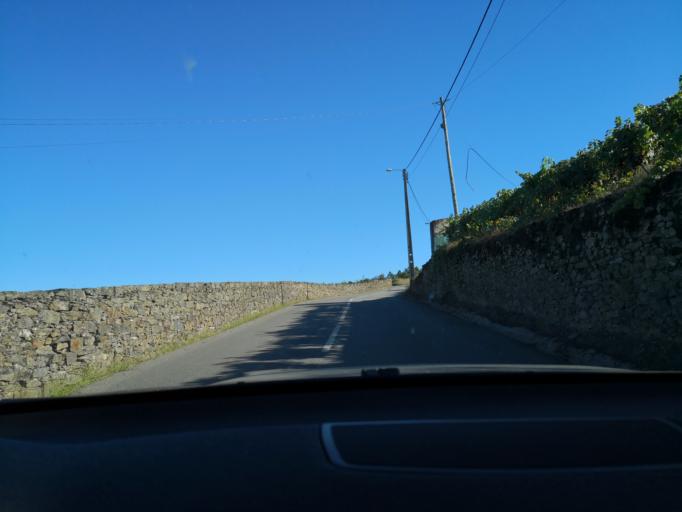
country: PT
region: Vila Real
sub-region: Sabrosa
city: Vilela
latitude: 41.2265
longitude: -7.5638
